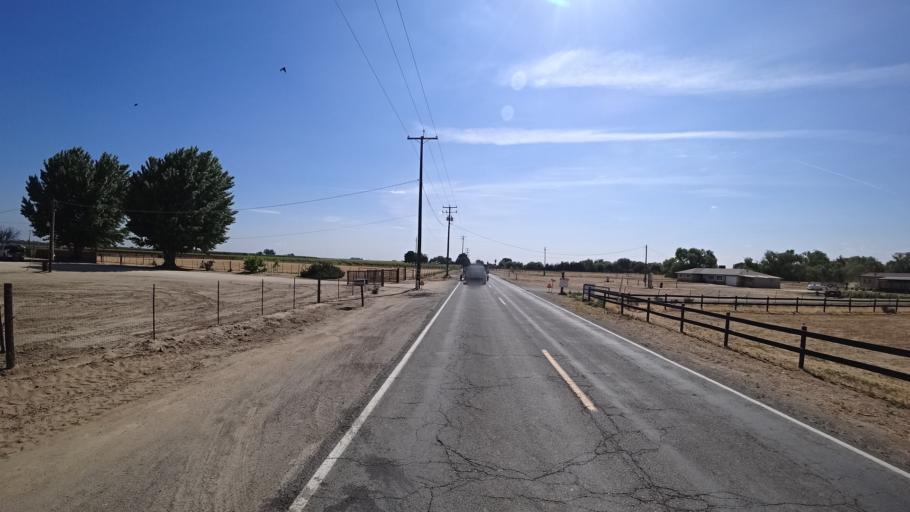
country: US
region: California
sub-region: Kings County
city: Lemoore
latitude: 36.2547
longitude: -119.7552
